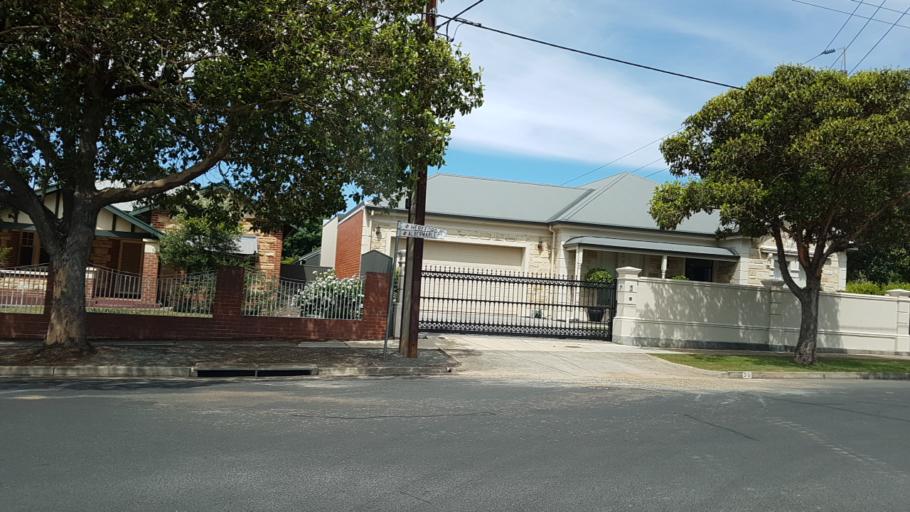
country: AU
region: South Australia
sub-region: Norwood Payneham St Peters
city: Trinity Gardens
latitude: -34.9118
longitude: 138.6484
